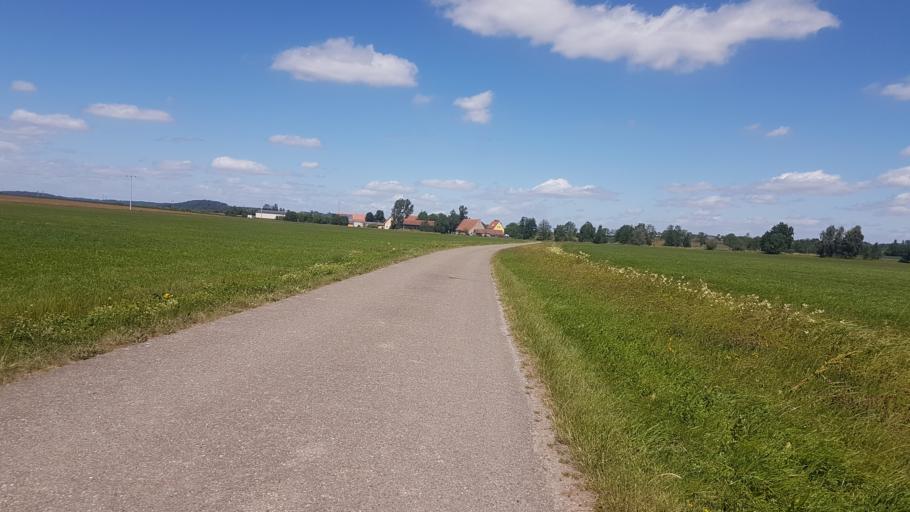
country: DE
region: Bavaria
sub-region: Regierungsbezirk Mittelfranken
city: Leutershausen
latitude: 49.2772
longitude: 10.4276
